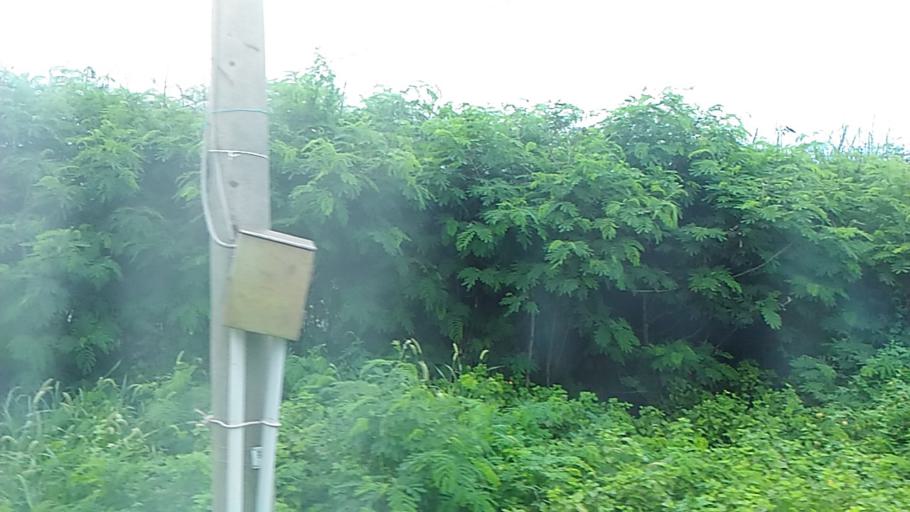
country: TW
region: Taiwan
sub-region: Penghu
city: Ma-kung
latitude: 23.2124
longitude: 119.4387
